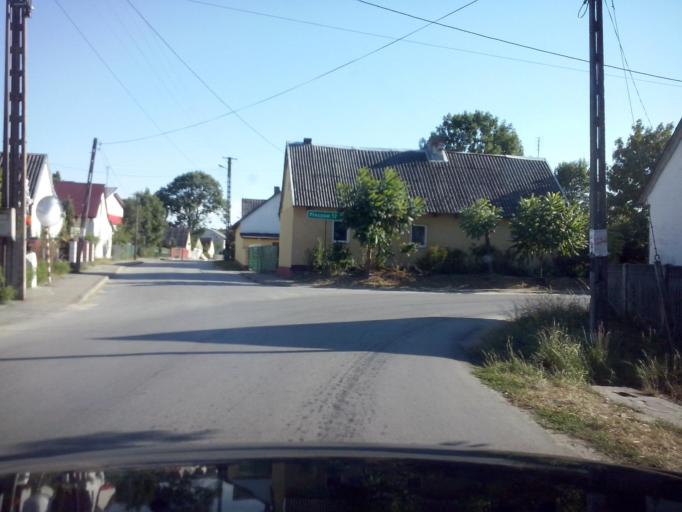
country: PL
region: Swietokrzyskie
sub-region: Powiat kielecki
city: Chmielnik
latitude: 50.5816
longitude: 20.7072
